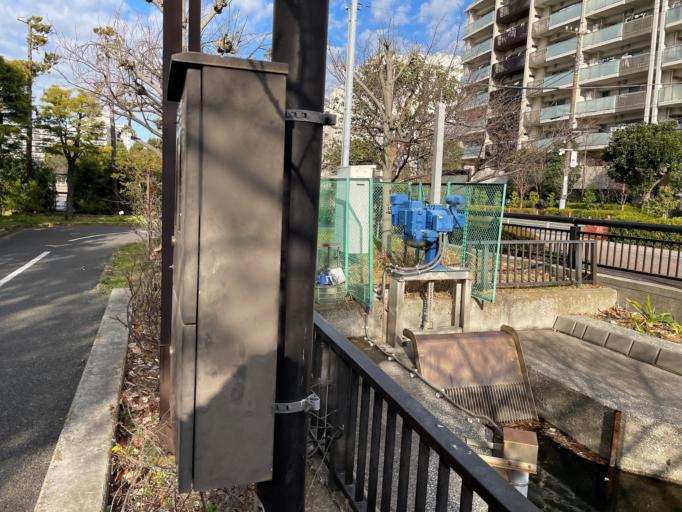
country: JP
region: Tokyo
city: Urayasu
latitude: 35.6746
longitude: 139.8362
